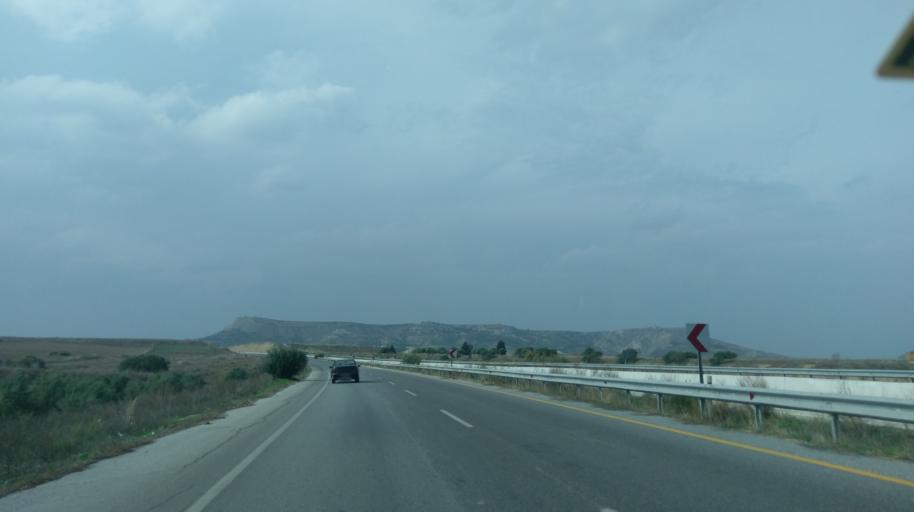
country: CY
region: Lefkosia
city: Mammari
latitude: 35.2220
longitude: 33.1575
